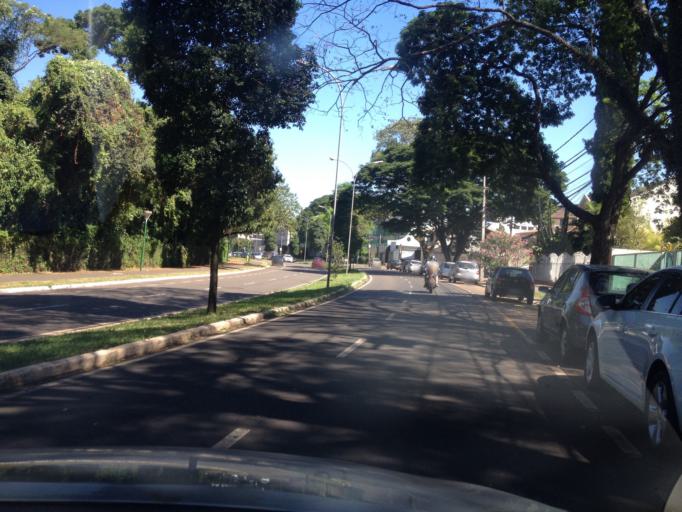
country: BR
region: Parana
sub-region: Maringa
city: Maringa
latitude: -23.4264
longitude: -51.9455
